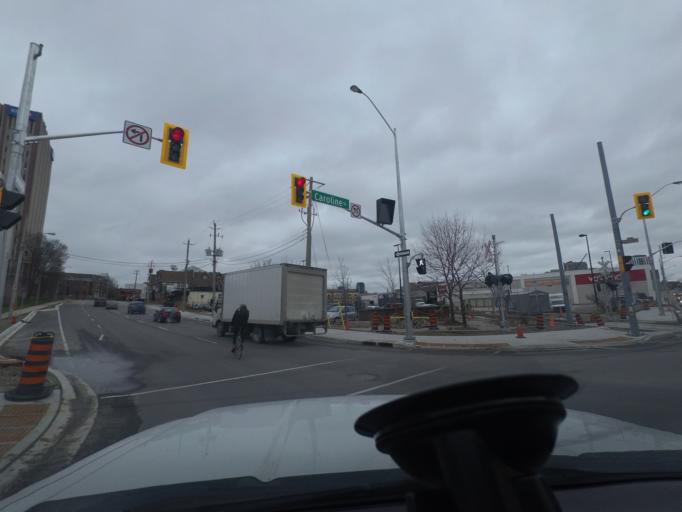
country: CN
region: Xinjiang Uygur Zizhiqu
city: Ayxin Siri
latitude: 43.4644
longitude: 80.5251
